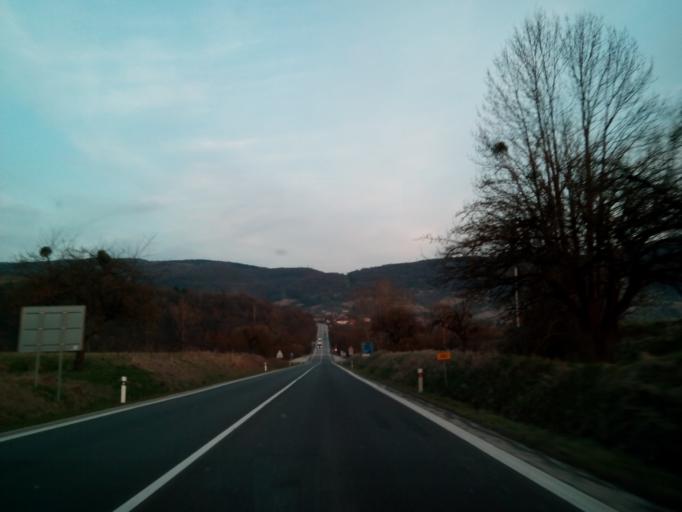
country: SK
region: Kosicky
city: Roznava
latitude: 48.6361
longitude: 20.6144
